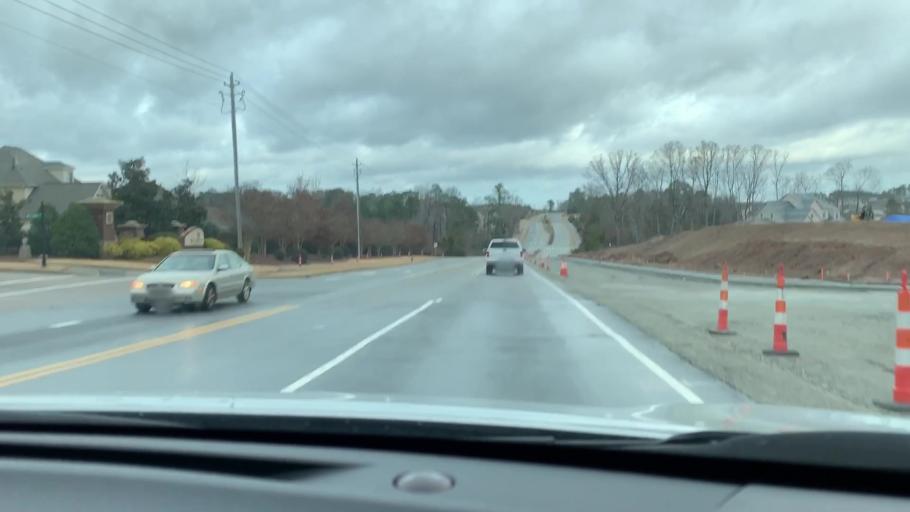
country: US
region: North Carolina
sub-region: Wake County
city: Green Level
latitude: 35.8349
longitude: -78.8995
